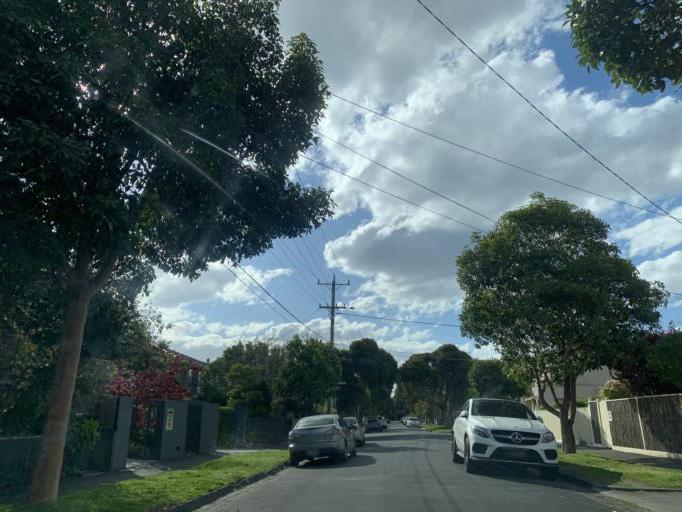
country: AU
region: Victoria
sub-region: Bayside
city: North Brighton
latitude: -37.9154
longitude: 145.0013
